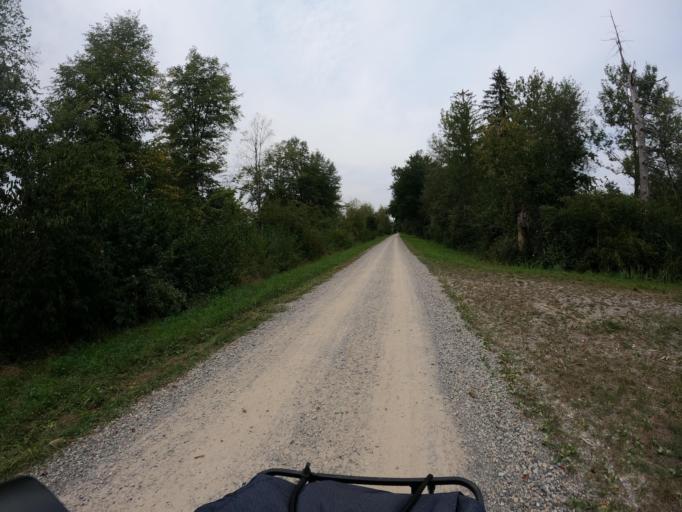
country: CH
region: Zurich
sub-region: Bezirk Affoltern
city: Ottenbach
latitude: 47.2739
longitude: 8.3975
